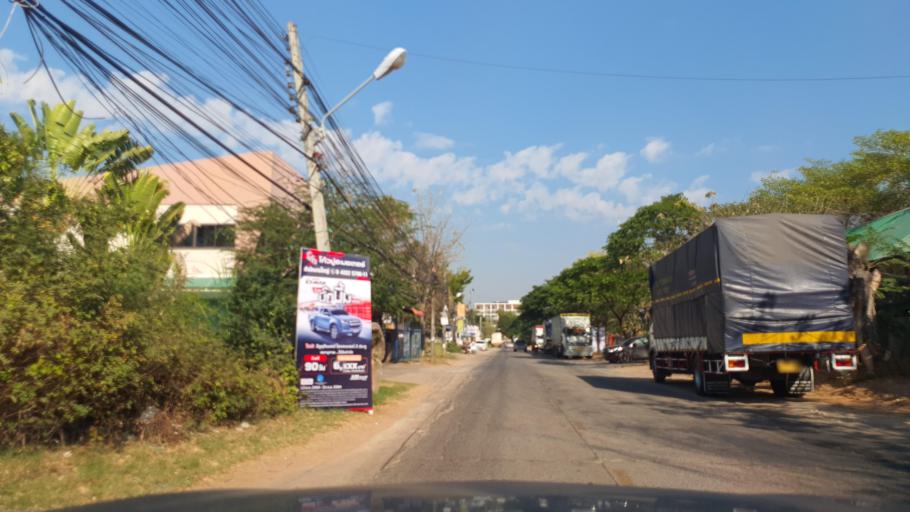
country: TH
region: Khon Kaen
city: Khon Kaen
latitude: 16.4358
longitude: 102.8144
